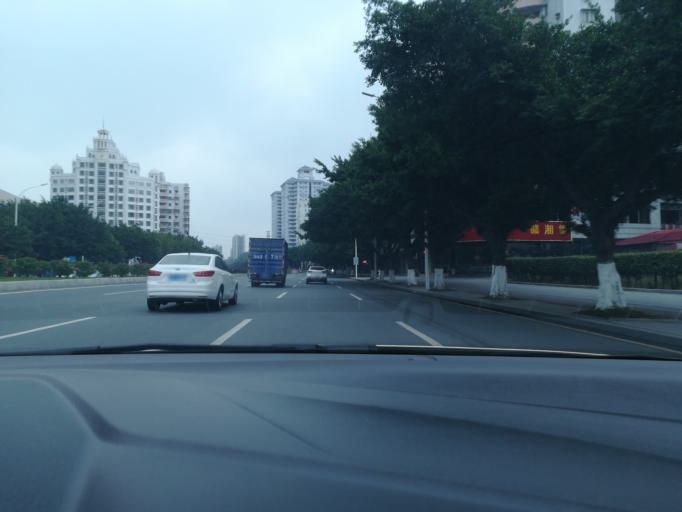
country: CN
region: Guangdong
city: Nansha
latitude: 22.8010
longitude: 113.5535
